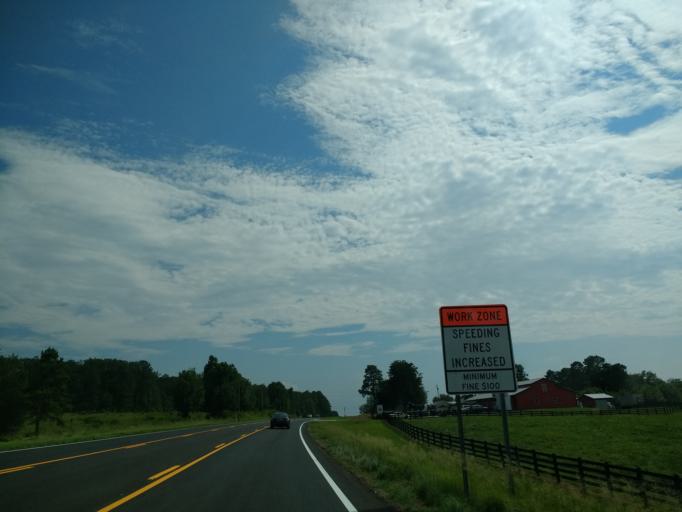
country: US
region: Georgia
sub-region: White County
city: Cleveland
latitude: 34.4923
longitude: -83.7568
